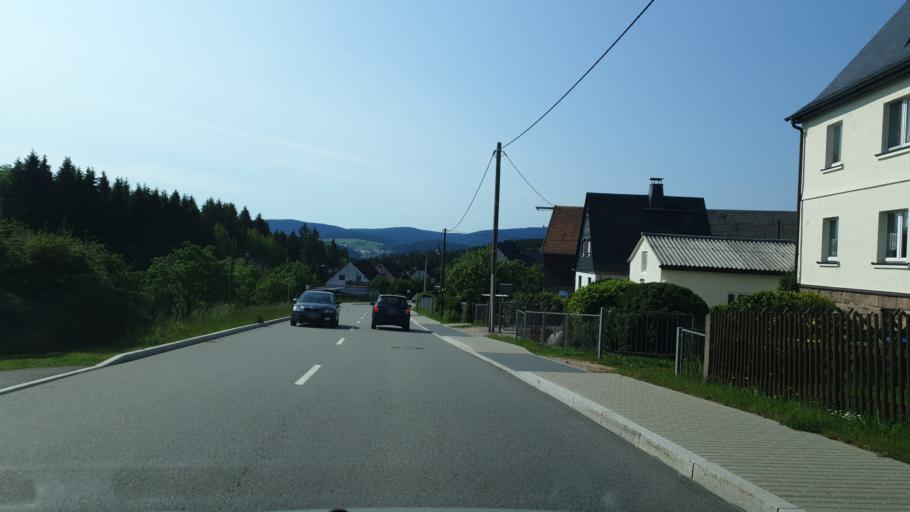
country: DE
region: Saxony
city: Zschorlau
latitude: 50.5341
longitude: 12.6207
